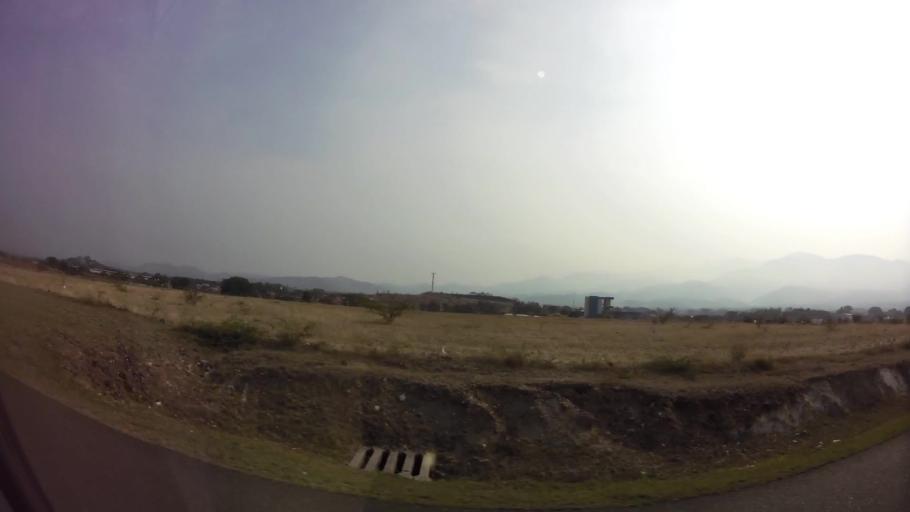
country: HN
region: Comayagua
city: Comayagua
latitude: 14.4268
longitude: -87.6367
